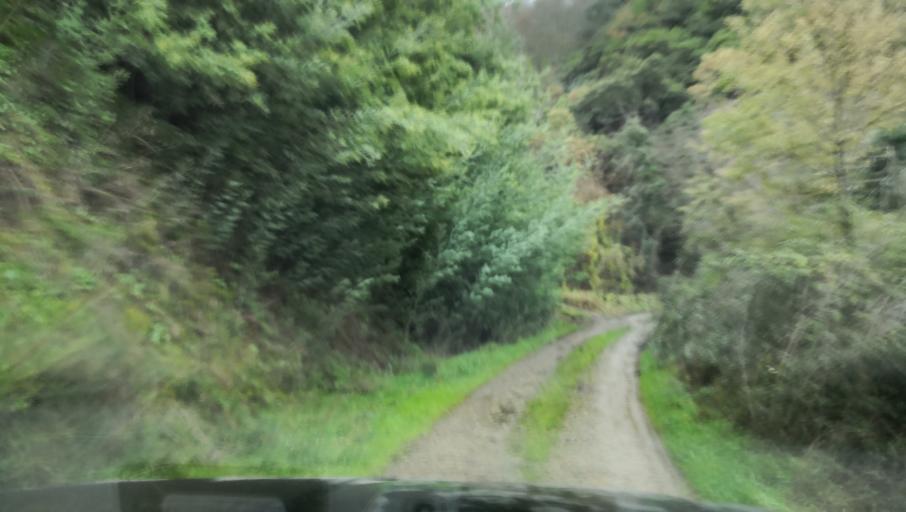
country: PT
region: Vila Real
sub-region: Vila Real
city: Vila Real
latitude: 41.2692
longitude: -7.7358
